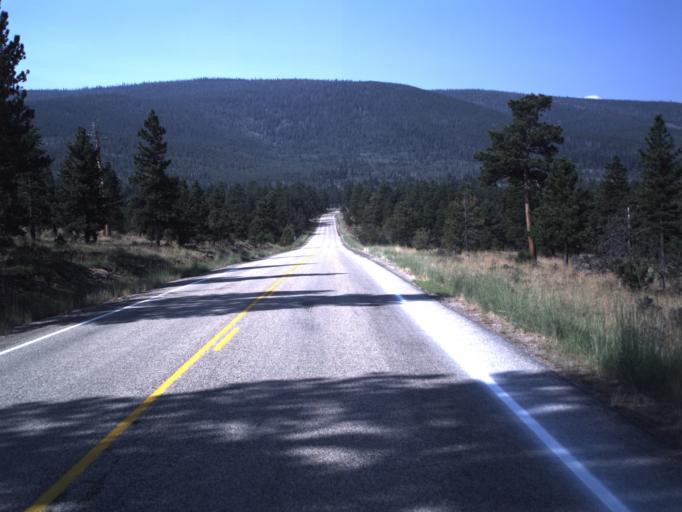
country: US
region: Utah
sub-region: Daggett County
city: Manila
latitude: 40.8708
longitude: -109.4712
